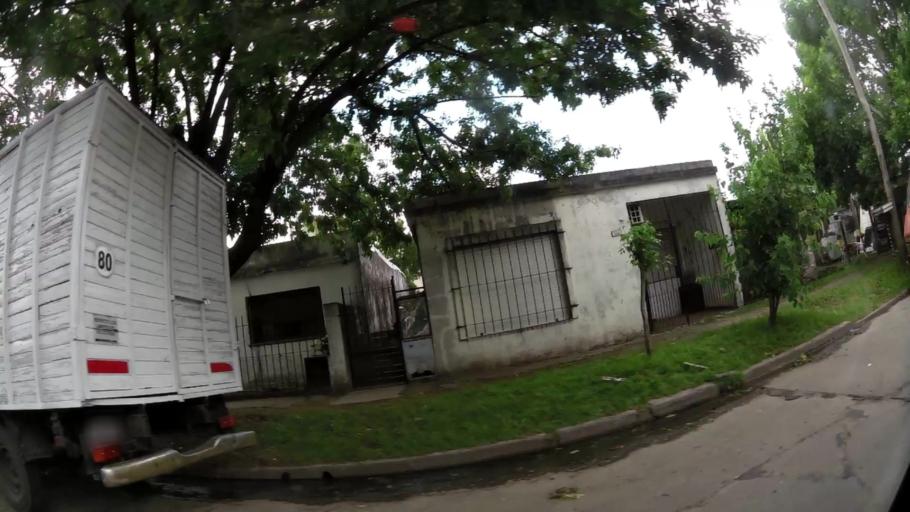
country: AR
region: Buenos Aires
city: Ituzaingo
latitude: -34.6422
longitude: -58.6793
